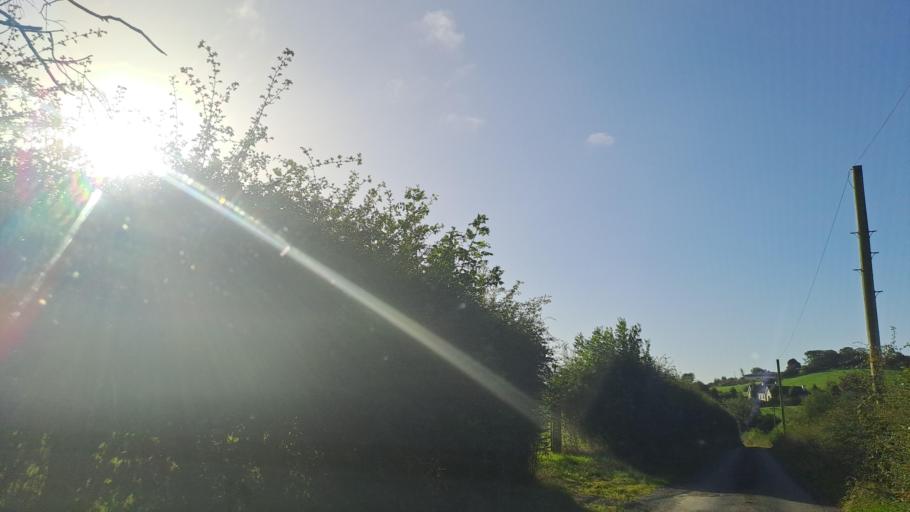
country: IE
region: Ulster
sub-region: An Cabhan
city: Kingscourt
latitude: 53.9489
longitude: -6.8772
